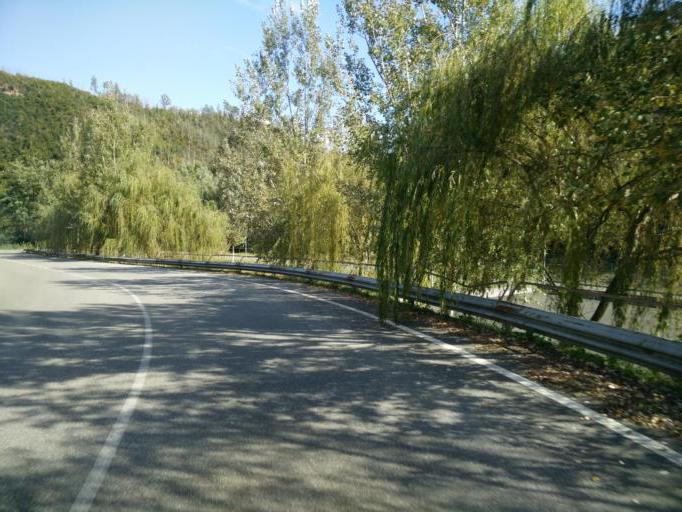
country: IT
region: Liguria
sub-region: Provincia di La Spezia
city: Carrodano
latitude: 44.2409
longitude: 9.6657
